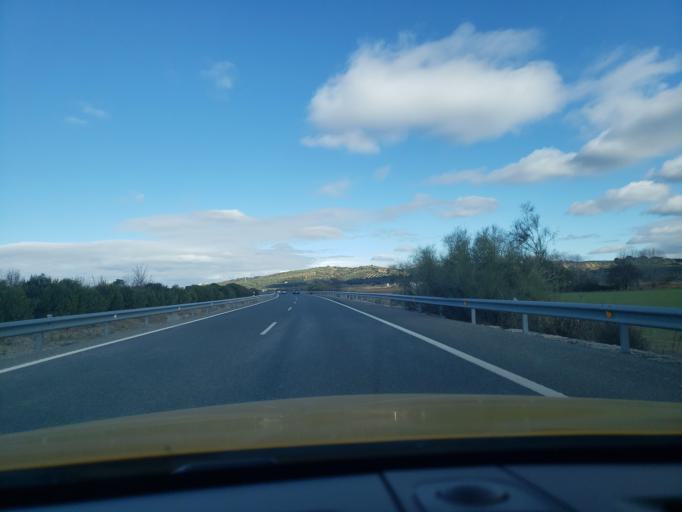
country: ES
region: Andalusia
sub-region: Provincia de Malaga
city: Villanueva del Trabuco
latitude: 37.0770
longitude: -4.3193
